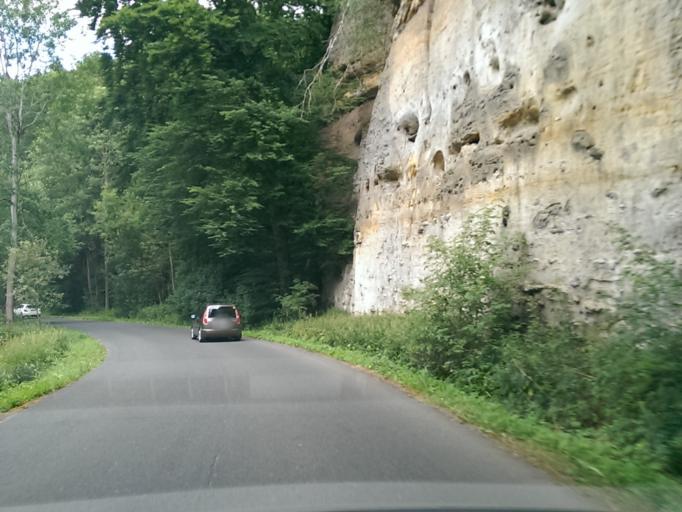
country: CZ
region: Central Bohemia
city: Mseno
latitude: 50.4137
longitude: 14.5805
